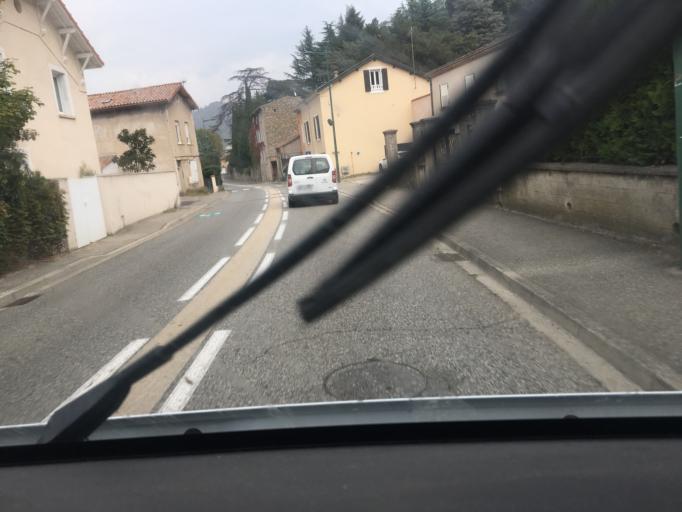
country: FR
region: Rhone-Alpes
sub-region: Departement de l'Ardeche
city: Saint-Jean-de-Muzols
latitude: 45.0701
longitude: 4.8193
